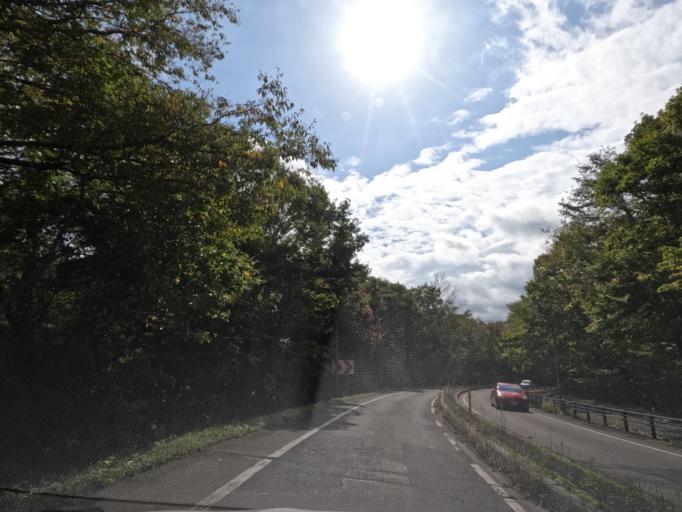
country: JP
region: Hokkaido
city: Chitose
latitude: 42.7976
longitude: 141.5673
